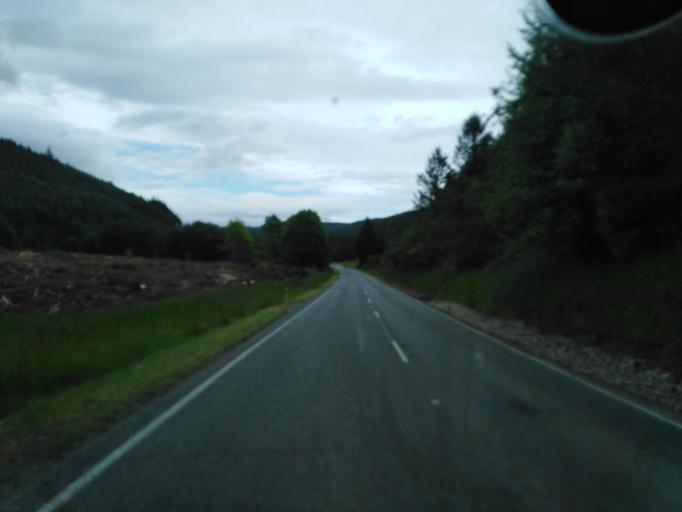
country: NZ
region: Tasman
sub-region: Tasman District
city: Wakefield
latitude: -41.4861
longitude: 172.8889
